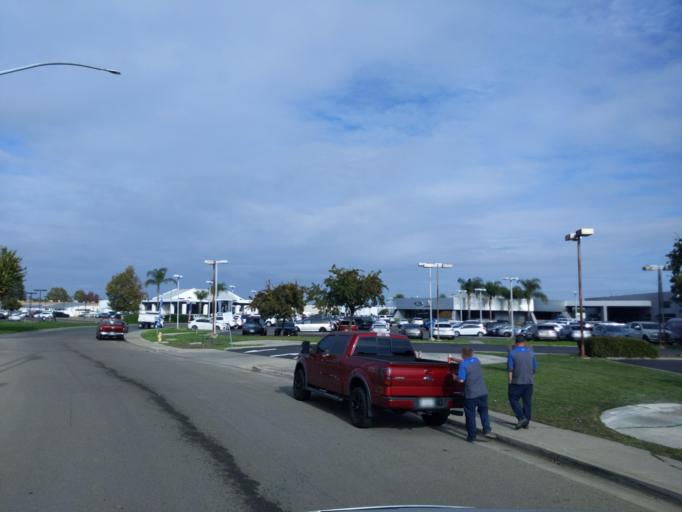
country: US
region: California
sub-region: San Joaquin County
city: Morada
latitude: 38.0179
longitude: -121.2762
